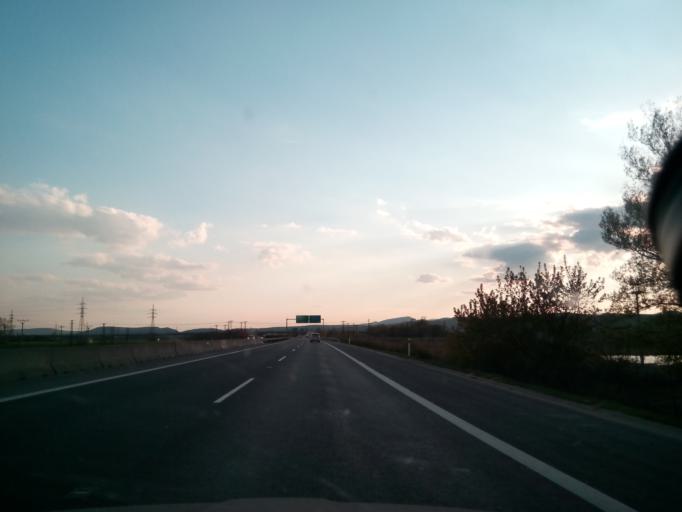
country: SK
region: Nitriansky
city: Dubnica nad Vahom
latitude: 48.9671
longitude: 18.1472
